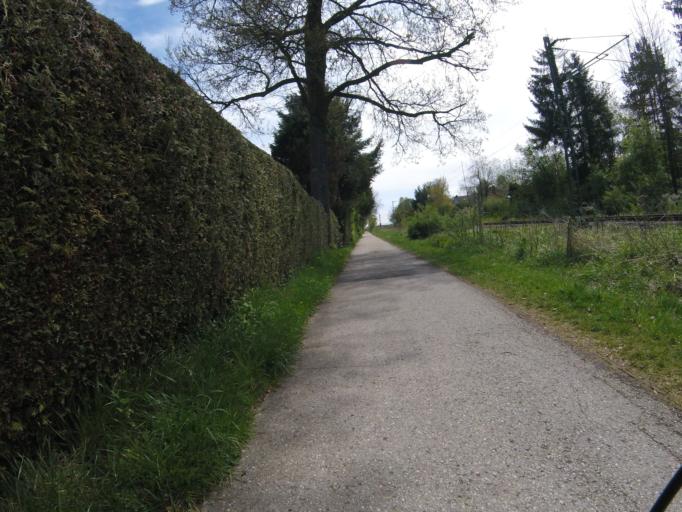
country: DE
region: Bavaria
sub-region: Upper Bavaria
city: Hohenbrunn
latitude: 48.0593
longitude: 11.6845
